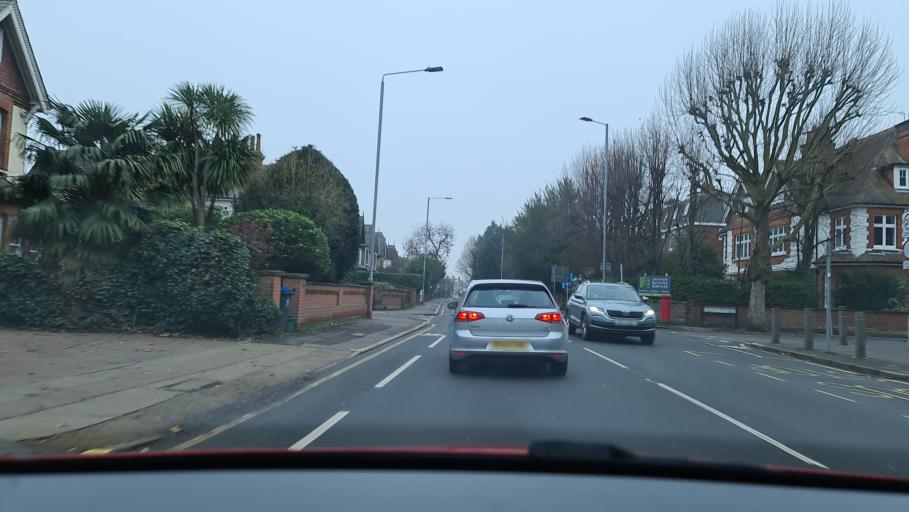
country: GB
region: England
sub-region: Greater London
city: Kingston upon Thames
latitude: 51.4226
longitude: -0.3030
